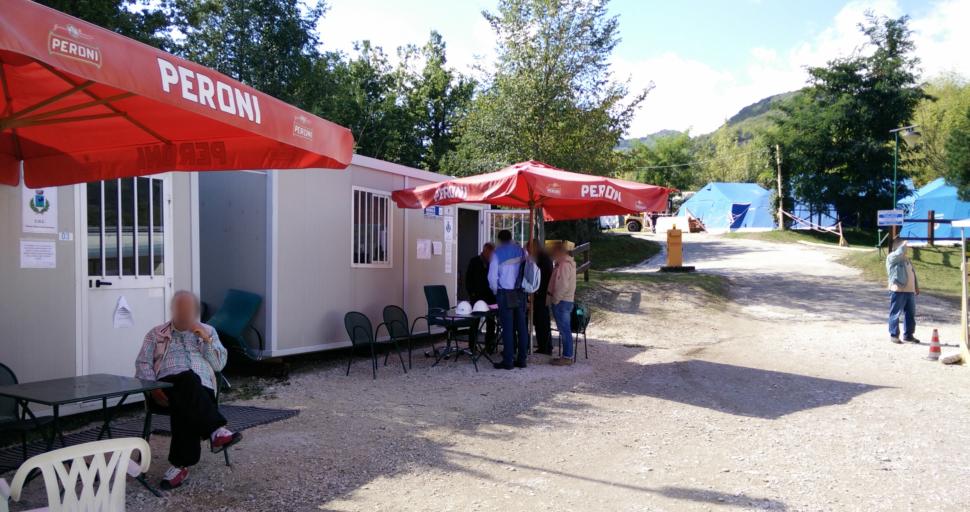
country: IT
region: The Marches
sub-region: Provincia di Ascoli Piceno
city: Balzo
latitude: 42.8391
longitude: 13.3307
